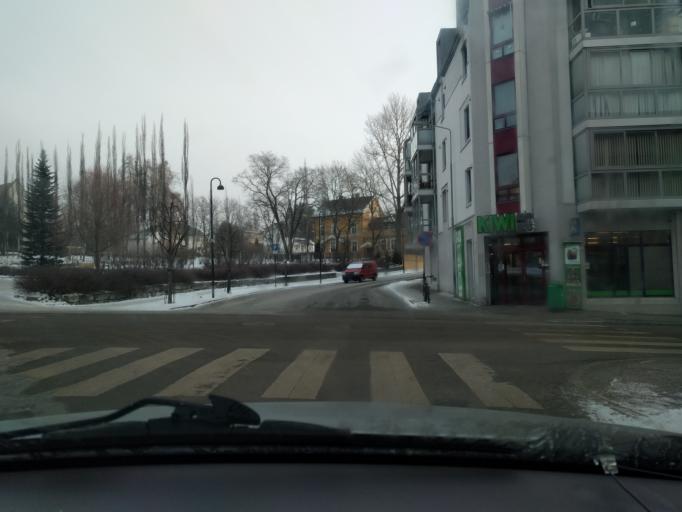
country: NO
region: Hedmark
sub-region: Hamar
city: Hamar
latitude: 60.7951
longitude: 11.0745
